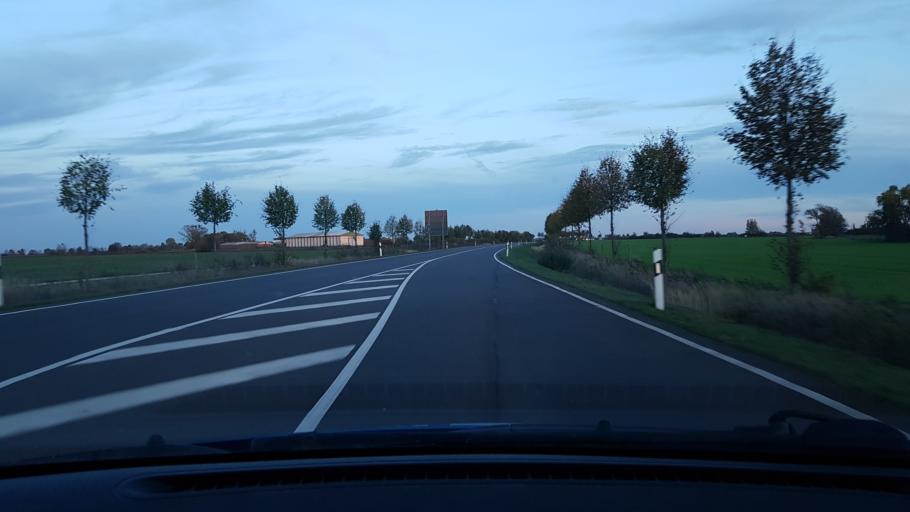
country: DE
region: Saxony-Anhalt
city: Gommern
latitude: 52.0845
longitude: 11.8316
